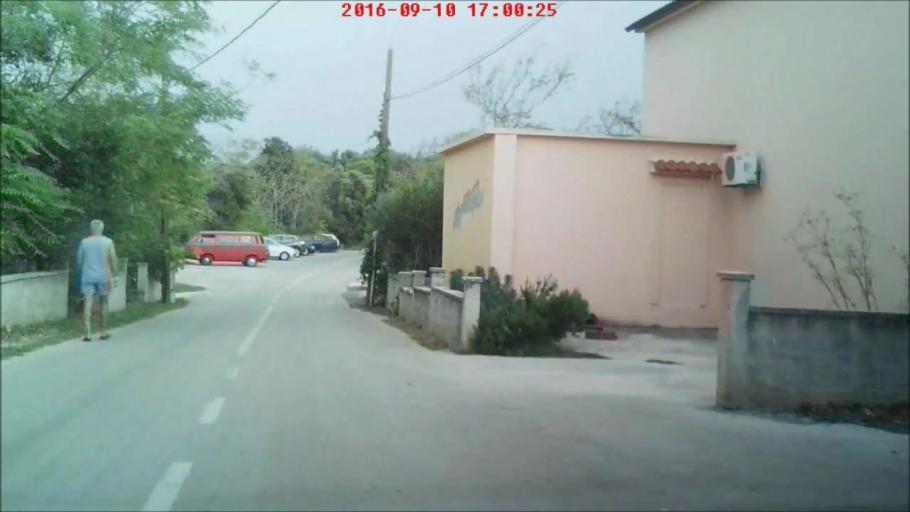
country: HR
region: Zadarska
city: Vir
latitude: 44.3097
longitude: 15.0572
